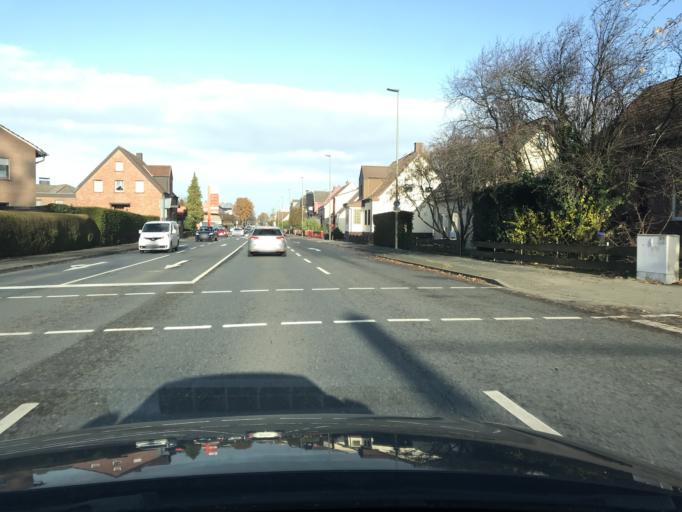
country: DE
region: North Rhine-Westphalia
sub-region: Regierungsbezirk Arnsberg
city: Hamm
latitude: 51.6447
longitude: 7.8436
